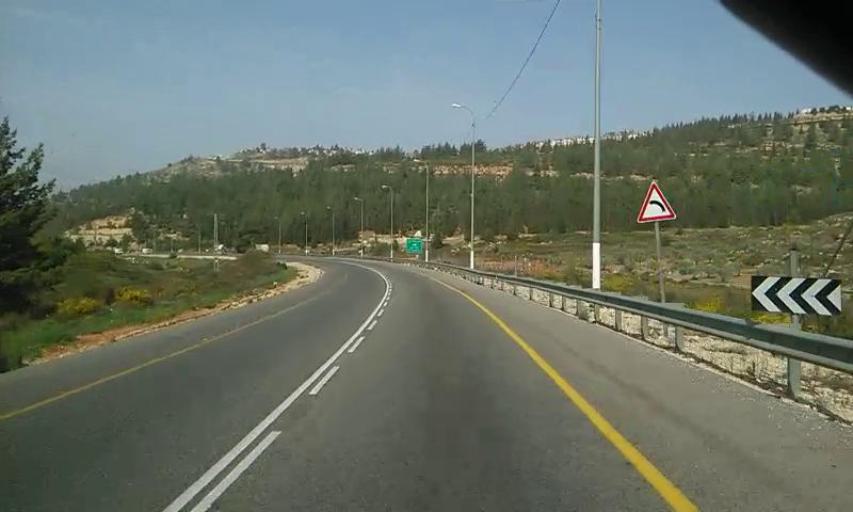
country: PS
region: West Bank
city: As Sawiyah
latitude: 32.0651
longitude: 35.2678
